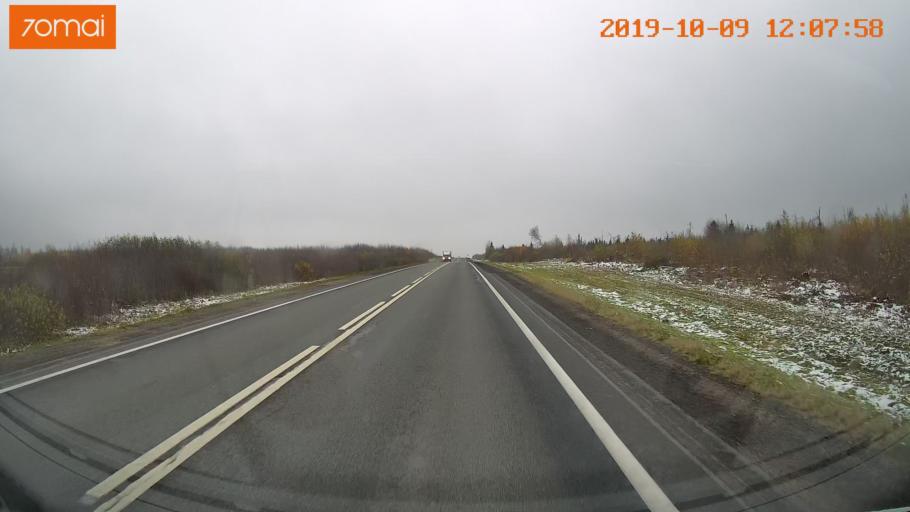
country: RU
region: Jaroslavl
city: Prechistoye
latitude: 58.5928
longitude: 40.3450
